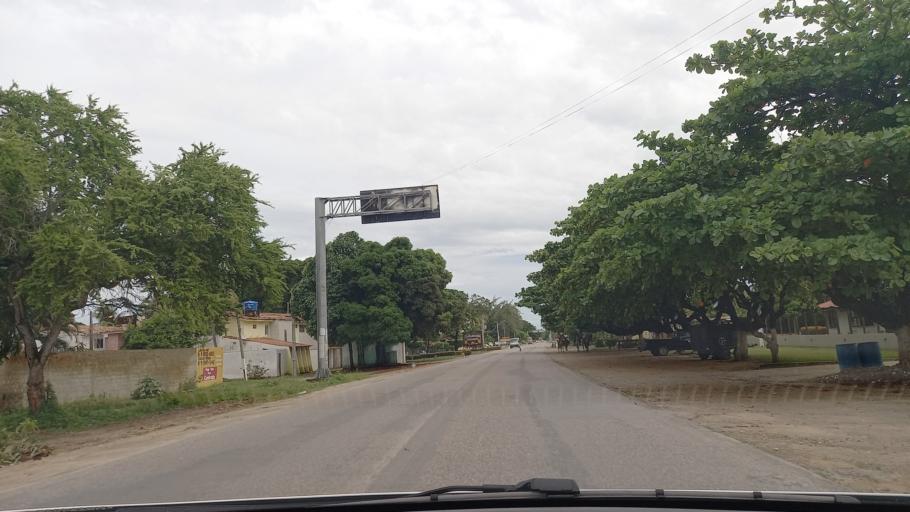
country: BR
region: Pernambuco
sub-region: Sao Jose Da Coroa Grande
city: Sao Jose da Coroa Grande
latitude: -8.9053
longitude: -35.1518
